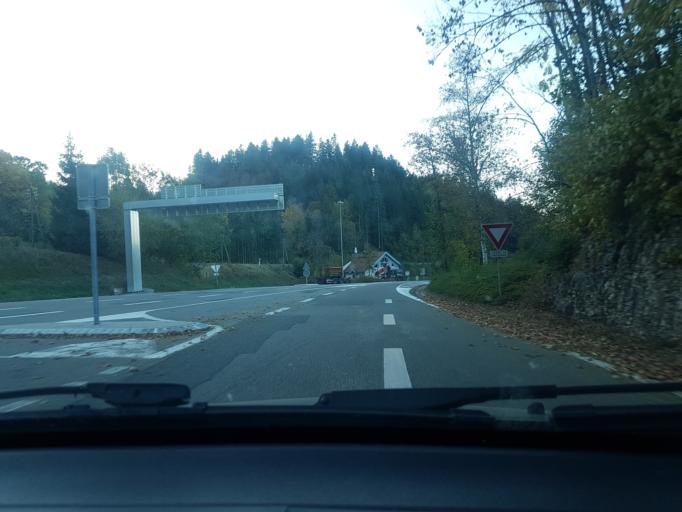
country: CH
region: Neuchatel
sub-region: Le Locle District
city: Les Brenets
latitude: 47.0530
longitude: 6.7099
